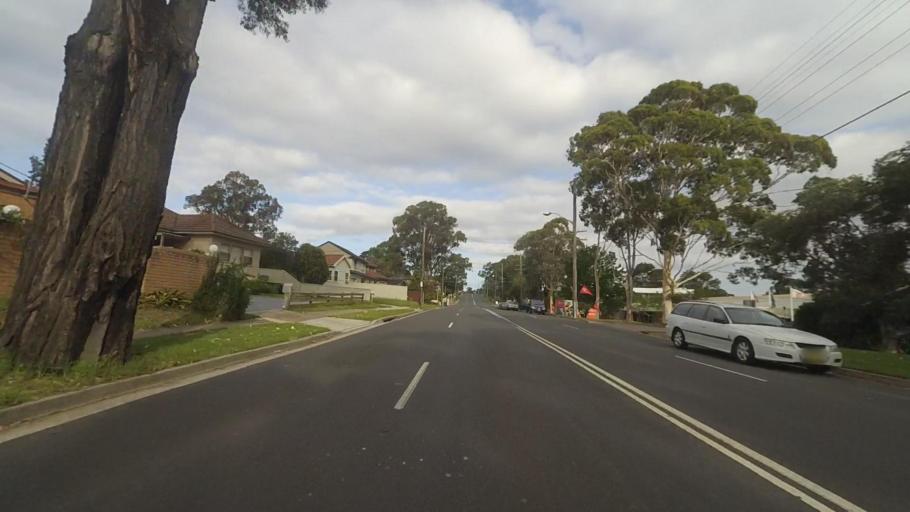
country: AU
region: New South Wales
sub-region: Bankstown
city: Milperra
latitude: -33.9160
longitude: 150.9999
